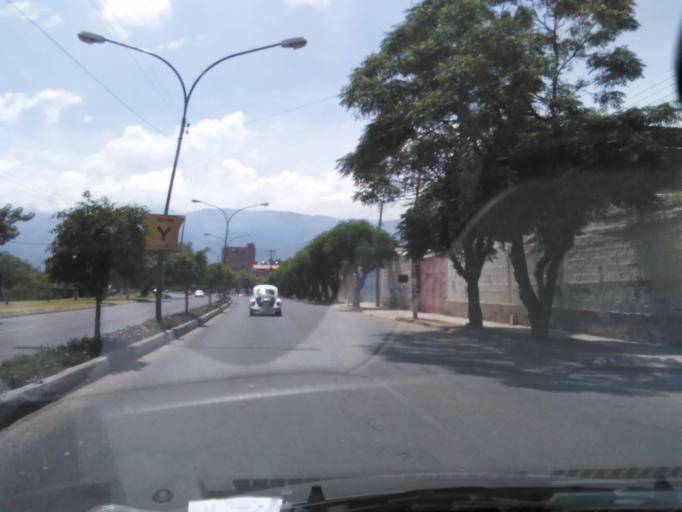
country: BO
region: Cochabamba
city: Cochabamba
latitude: -17.4034
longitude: -66.1690
